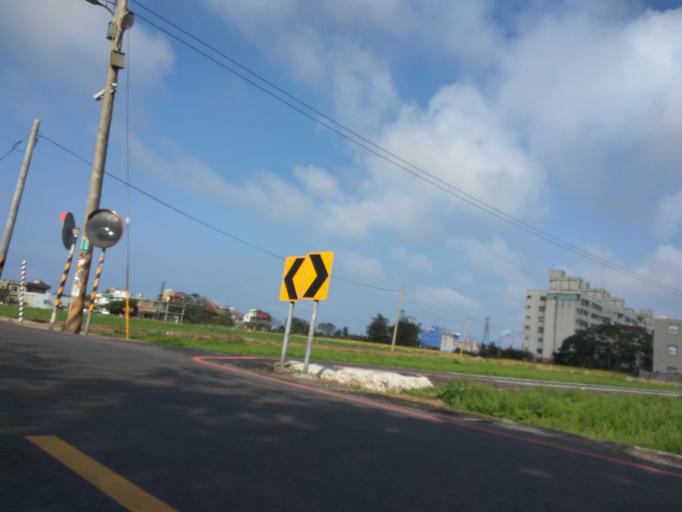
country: TW
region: Taiwan
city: Taoyuan City
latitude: 25.0623
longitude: 121.1733
